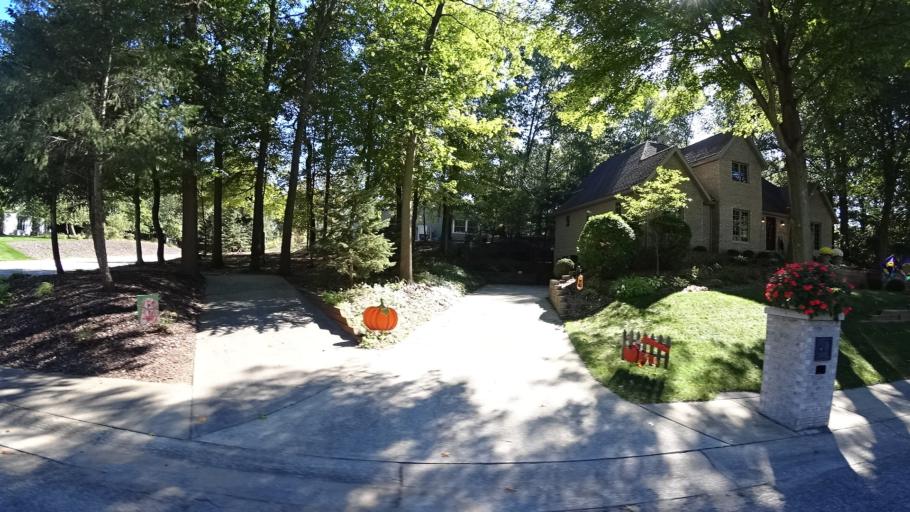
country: US
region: Indiana
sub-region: LaPorte County
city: Long Beach
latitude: 41.7471
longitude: -86.8303
